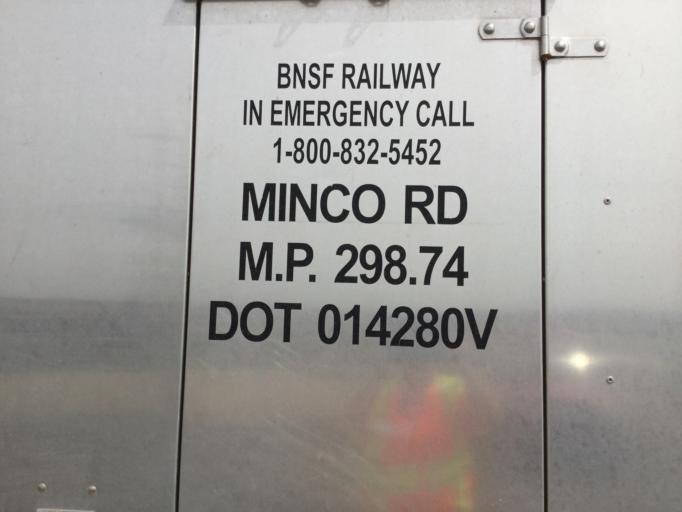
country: US
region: Kansas
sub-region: Barber County
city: Kiowa
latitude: 37.1039
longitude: -98.3934
